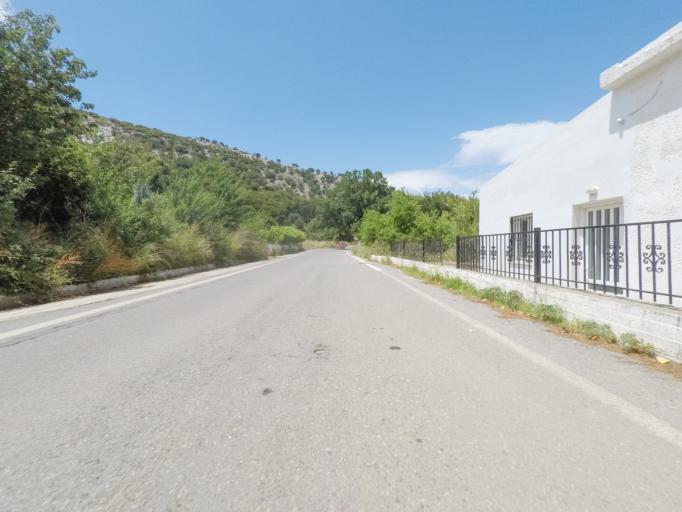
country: GR
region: Crete
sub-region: Nomos Irakleiou
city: Mokhos
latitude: 35.1716
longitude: 25.4374
